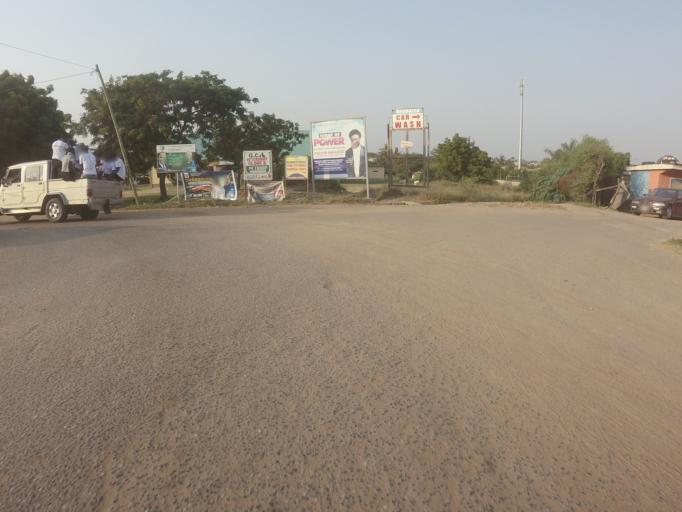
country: GH
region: Greater Accra
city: Nungua
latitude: 5.6168
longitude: -0.0477
